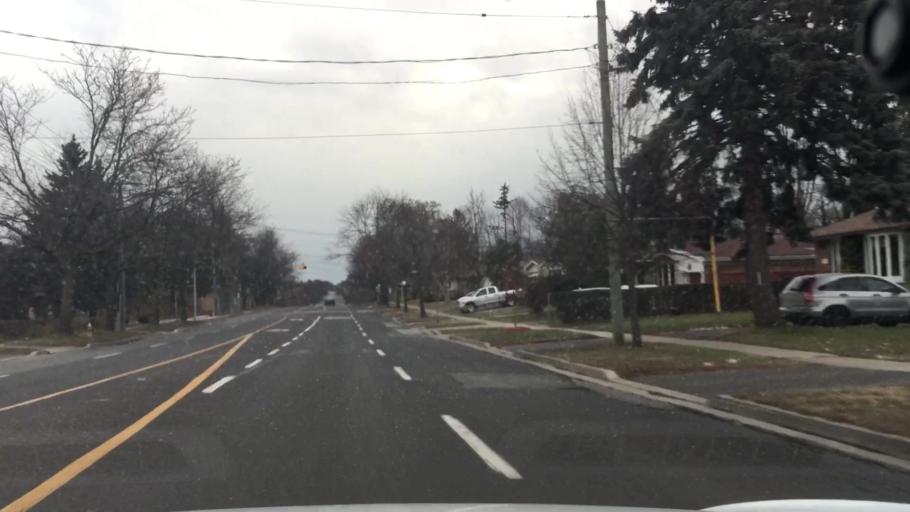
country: CA
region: Ontario
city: Scarborough
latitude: 43.7563
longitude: -79.2352
